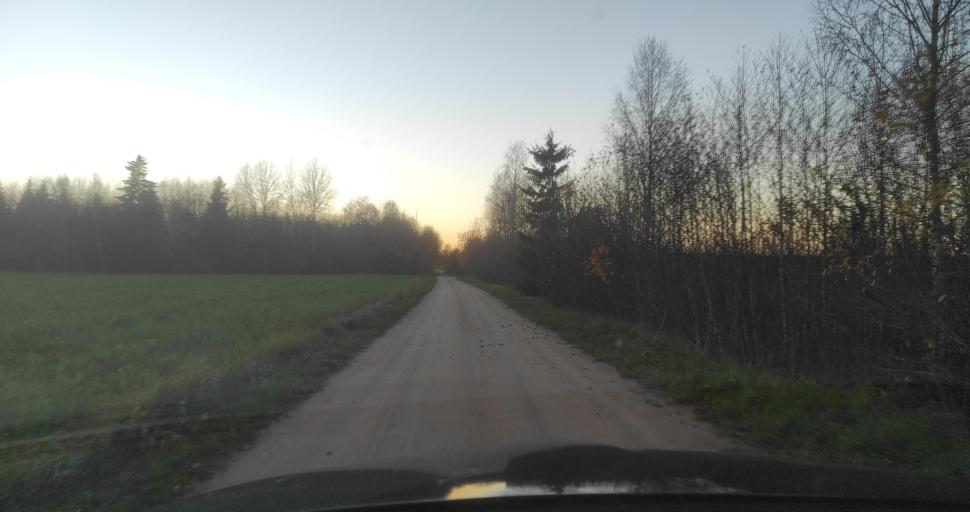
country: LV
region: Saldus Rajons
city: Saldus
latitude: 56.8033
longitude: 22.2773
